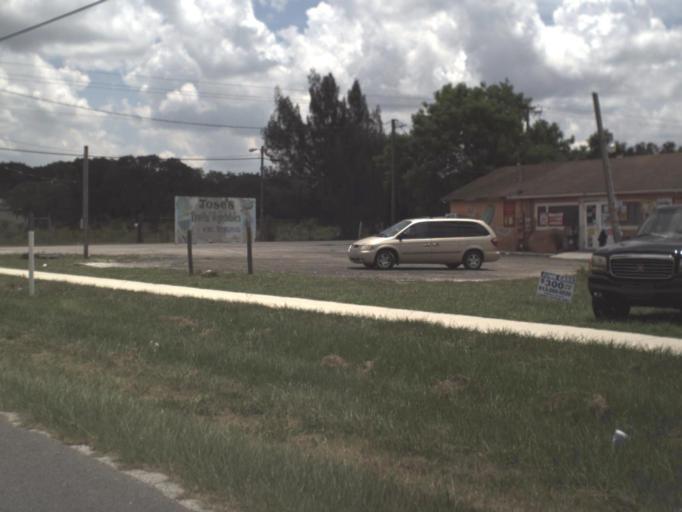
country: US
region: Florida
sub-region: Hillsborough County
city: Wimauma
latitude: 27.7125
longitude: -82.3196
